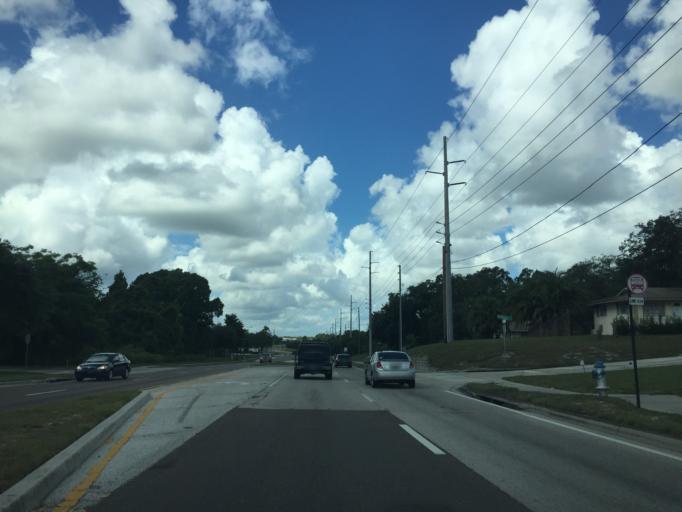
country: US
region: Florida
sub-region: Seminole County
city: Oviedo
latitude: 28.6558
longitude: -81.2095
